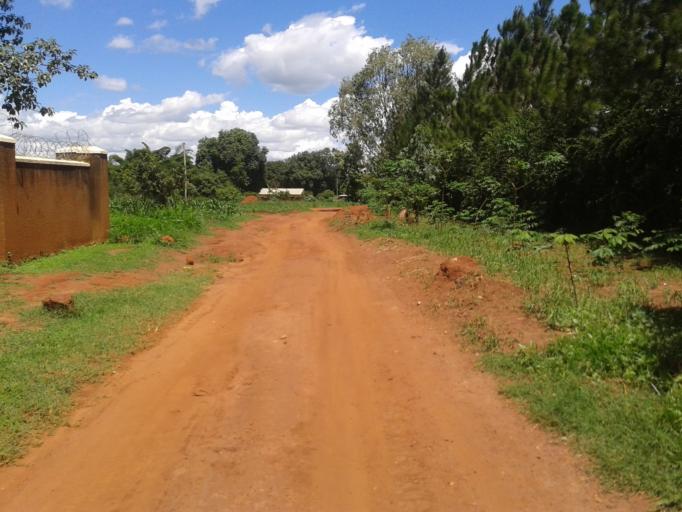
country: UG
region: Northern Region
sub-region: Gulu District
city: Gulu
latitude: 2.7719
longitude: 32.3199
